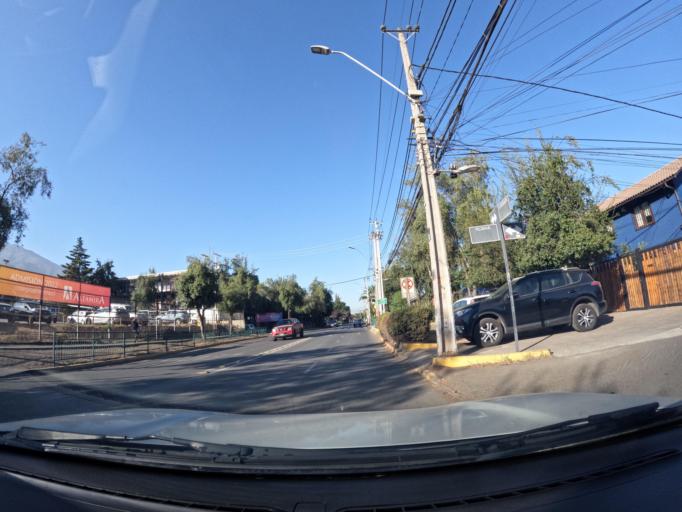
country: CL
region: Santiago Metropolitan
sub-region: Provincia de Santiago
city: Villa Presidente Frei, Nunoa, Santiago, Chile
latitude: -33.4786
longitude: -70.5383
